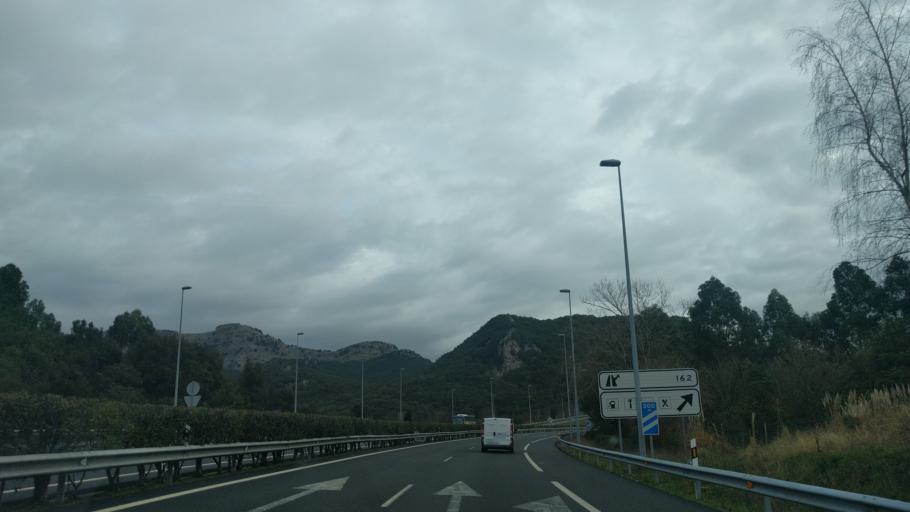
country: ES
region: Cantabria
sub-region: Provincia de Cantabria
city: Liendo
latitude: 43.3900
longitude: -3.3588
